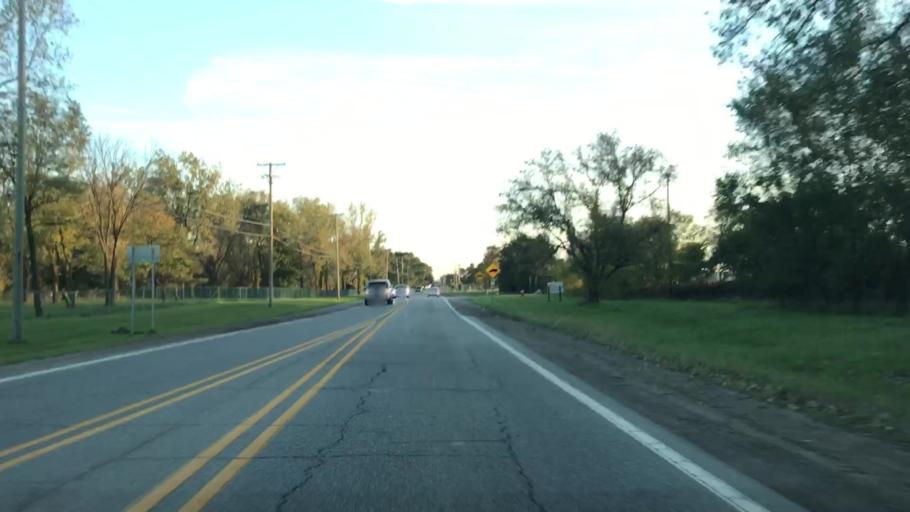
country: US
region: Michigan
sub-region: Macomb County
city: Shelby
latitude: 42.6494
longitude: -83.0730
